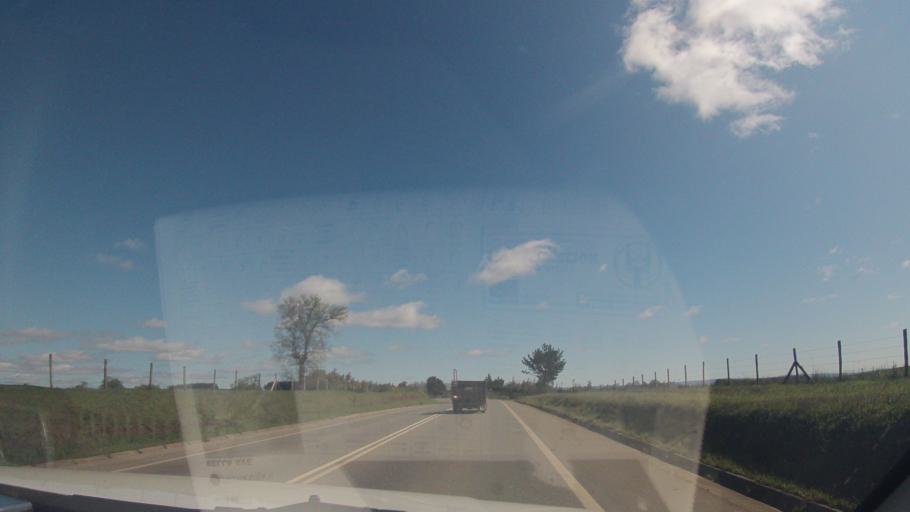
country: CL
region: Araucania
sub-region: Provincia de Malleco
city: Traiguen
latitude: -38.2015
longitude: -72.7790
